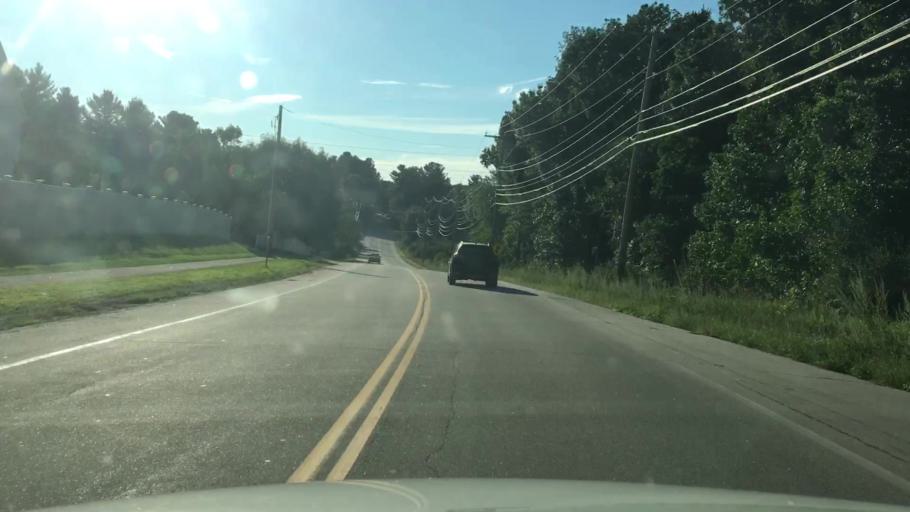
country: US
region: New Hampshire
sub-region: Strafford County
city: Dover
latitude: 43.1664
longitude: -70.8473
